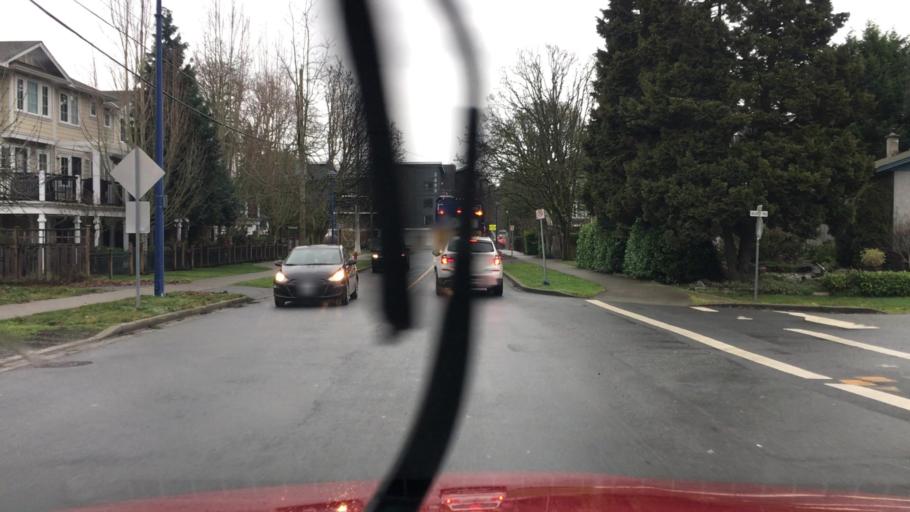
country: CA
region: British Columbia
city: Langford
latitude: 48.4532
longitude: -123.5003
